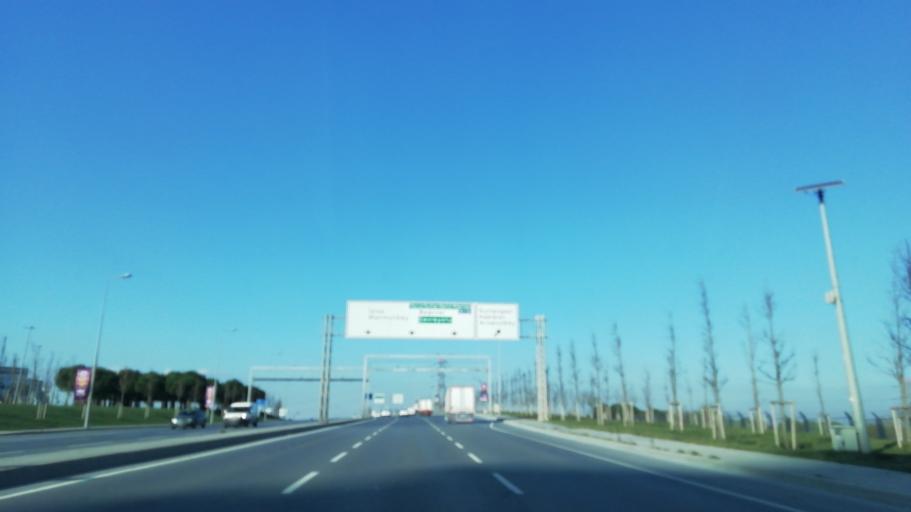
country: TR
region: Istanbul
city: Mahmutbey
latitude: 41.0668
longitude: 28.8384
